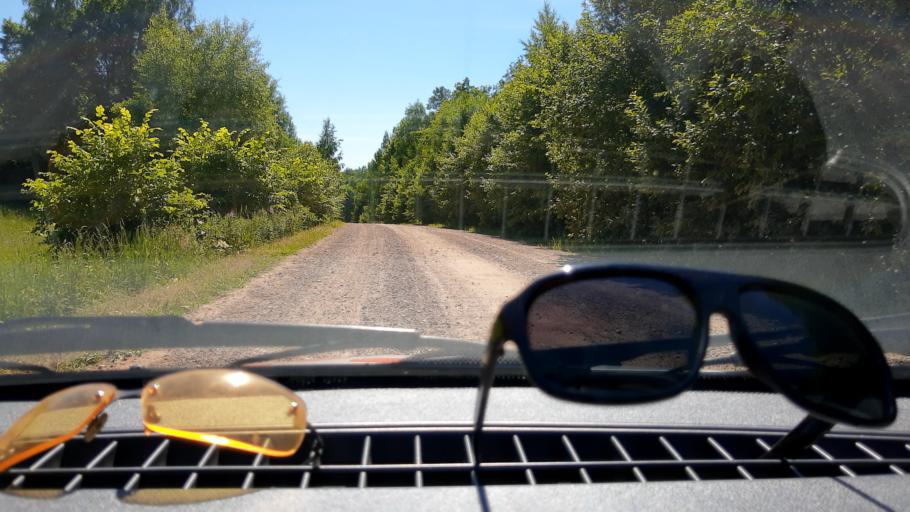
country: RU
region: Bashkortostan
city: Ulu-Telyak
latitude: 54.7843
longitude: 56.9919
